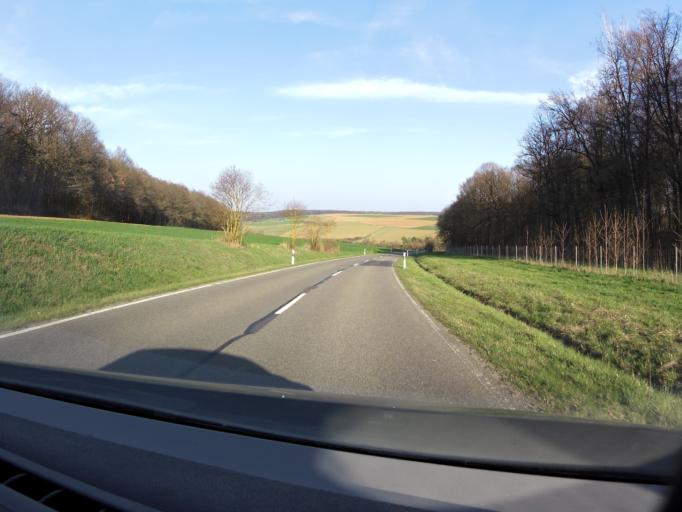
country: DE
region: Baden-Wuerttemberg
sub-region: Regierungsbezirk Stuttgart
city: Grunsfeld
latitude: 49.5834
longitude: 9.8032
